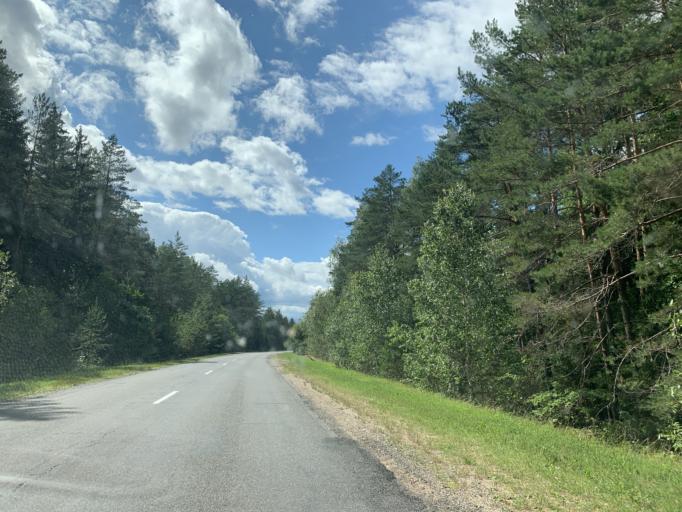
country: BY
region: Minsk
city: Rakaw
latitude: 53.9863
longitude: 26.9349
